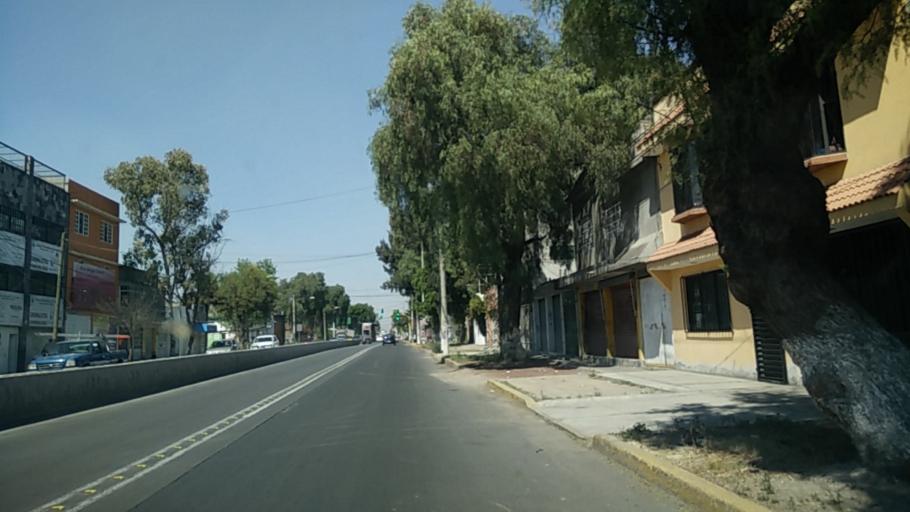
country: MX
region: Mexico
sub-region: Atenco
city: Colonia el Salado
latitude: 19.5920
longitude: -99.0283
